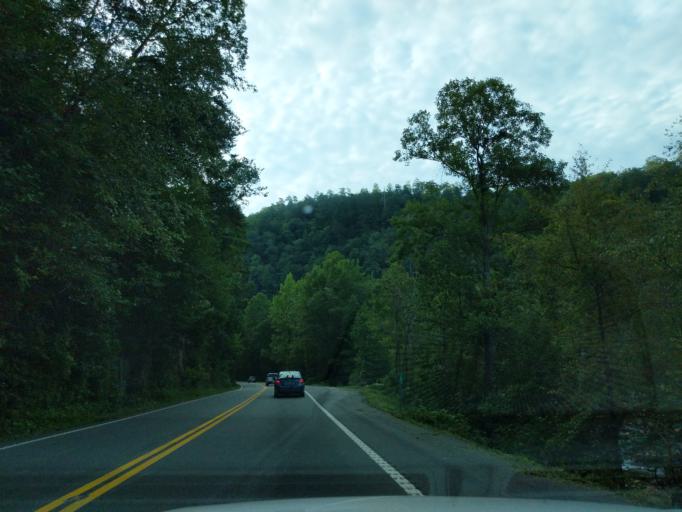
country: US
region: Georgia
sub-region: Fannin County
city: McCaysville
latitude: 35.0744
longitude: -84.5072
